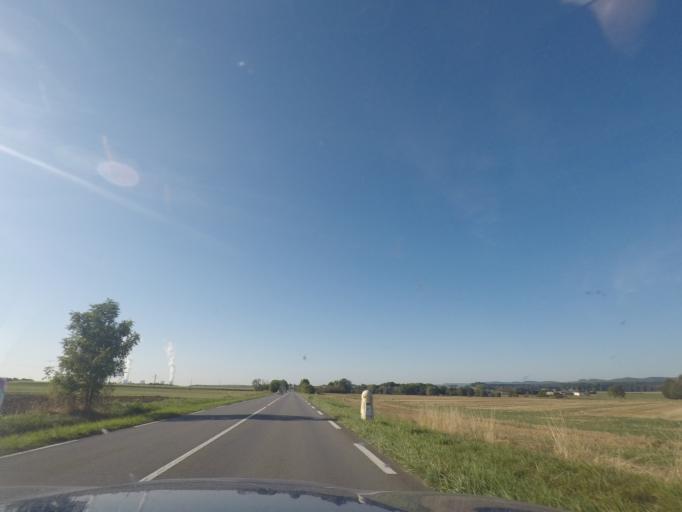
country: LU
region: Luxembourg
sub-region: Canton d'Esch-sur-Alzette
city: Frisange
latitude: 49.4952
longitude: 6.1935
